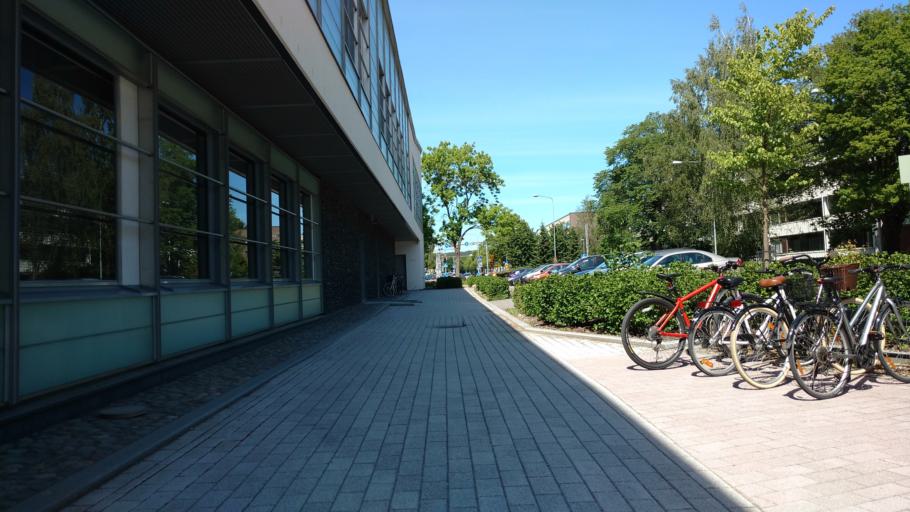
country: FI
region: Varsinais-Suomi
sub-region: Salo
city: Salo
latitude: 60.3824
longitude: 23.1299
